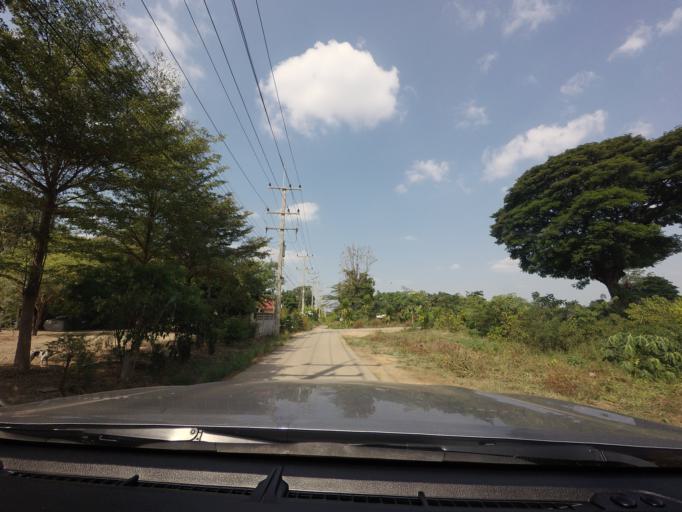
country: TH
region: Phitsanulok
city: Phitsanulok
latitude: 16.8195
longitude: 100.2352
